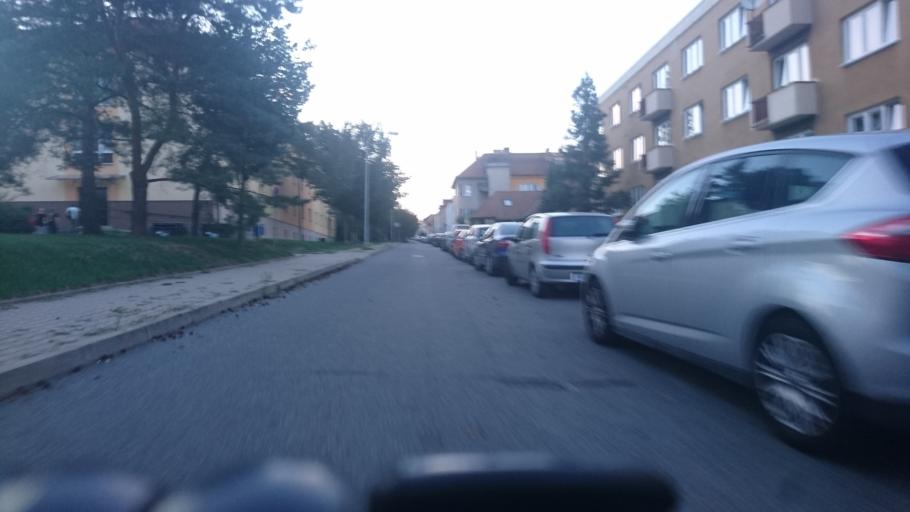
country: CZ
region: South Moravian
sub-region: Mesto Brno
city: Mokra Hora
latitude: 49.2422
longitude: 16.5812
